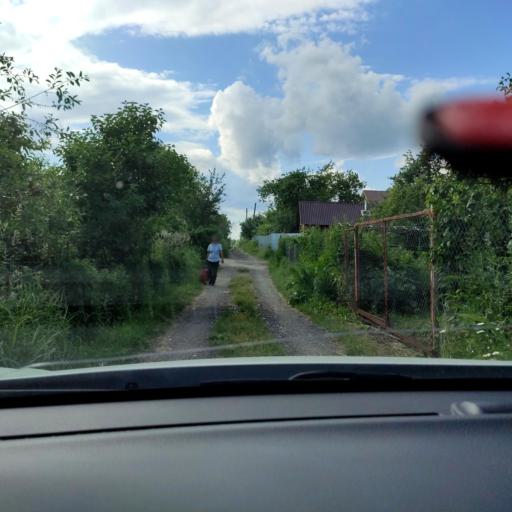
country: RU
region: Tatarstan
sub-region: Gorod Kazan'
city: Kazan
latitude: 55.8902
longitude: 49.0606
